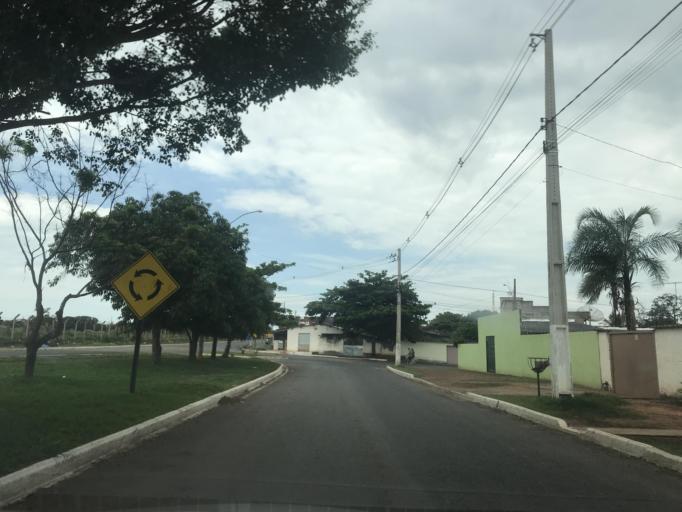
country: BR
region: Goias
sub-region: Luziania
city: Luziania
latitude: -16.2567
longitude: -47.9647
